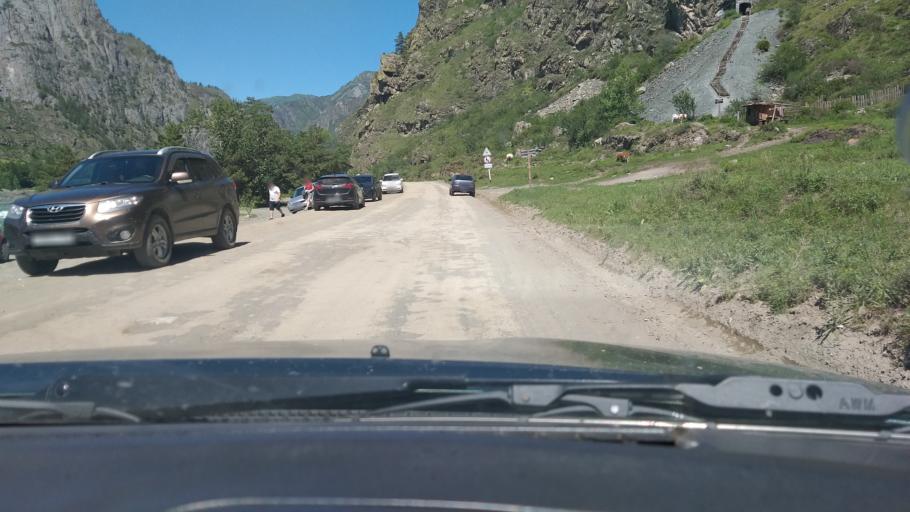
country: RU
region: Altay
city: Chemal
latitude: 51.1998
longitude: 86.0853
